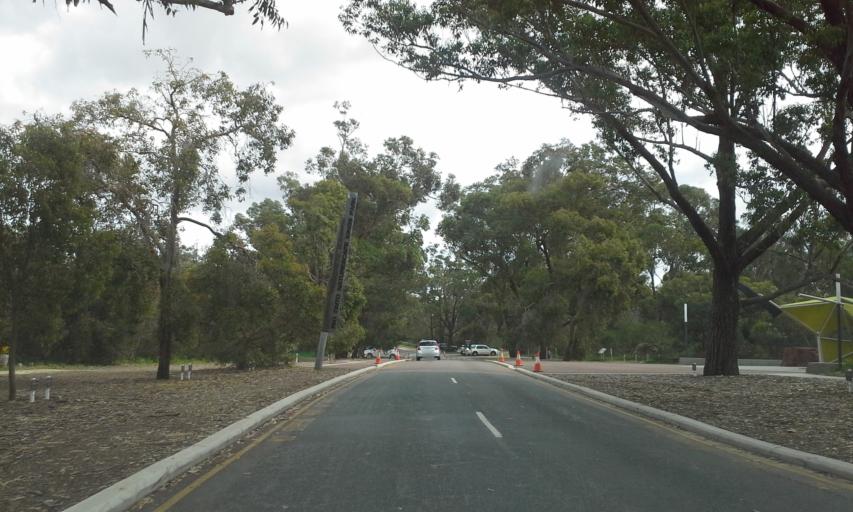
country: AU
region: Western Australia
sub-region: City of Perth
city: West Perth
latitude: -31.9590
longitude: 115.8398
